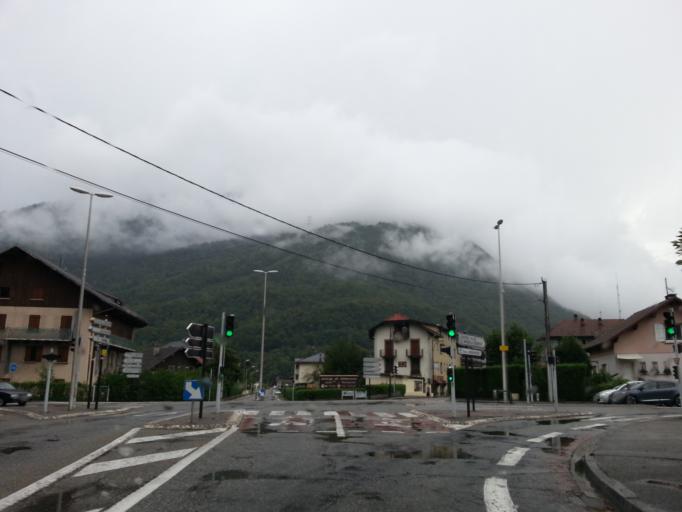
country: FR
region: Rhone-Alpes
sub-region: Departement de la Savoie
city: Albertville
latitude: 45.6686
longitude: 6.3946
